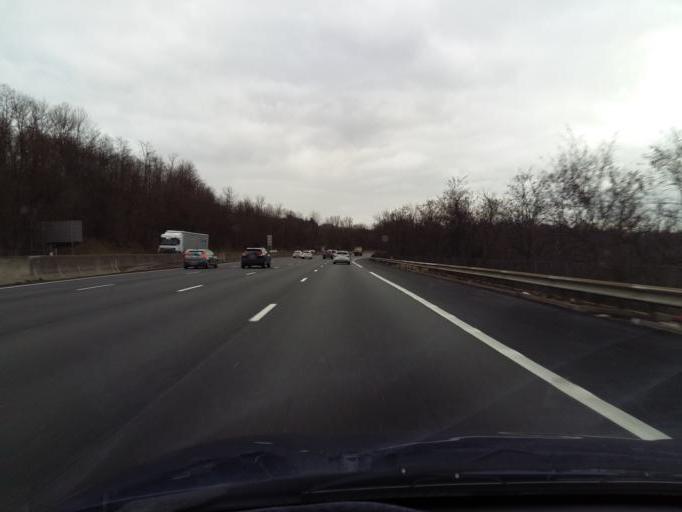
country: FR
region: Rhone-Alpes
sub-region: Departement de l'Isere
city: Reventin-Vaugris
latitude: 45.4868
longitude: 4.8336
